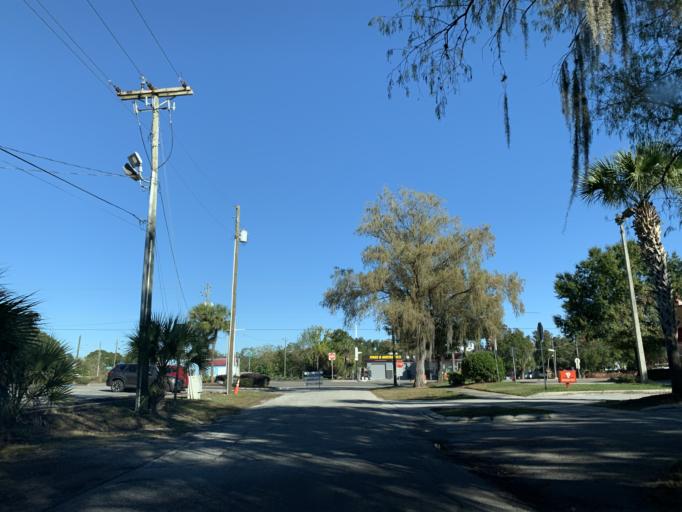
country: US
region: Florida
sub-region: Hillsborough County
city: University
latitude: 28.0319
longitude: -82.4290
